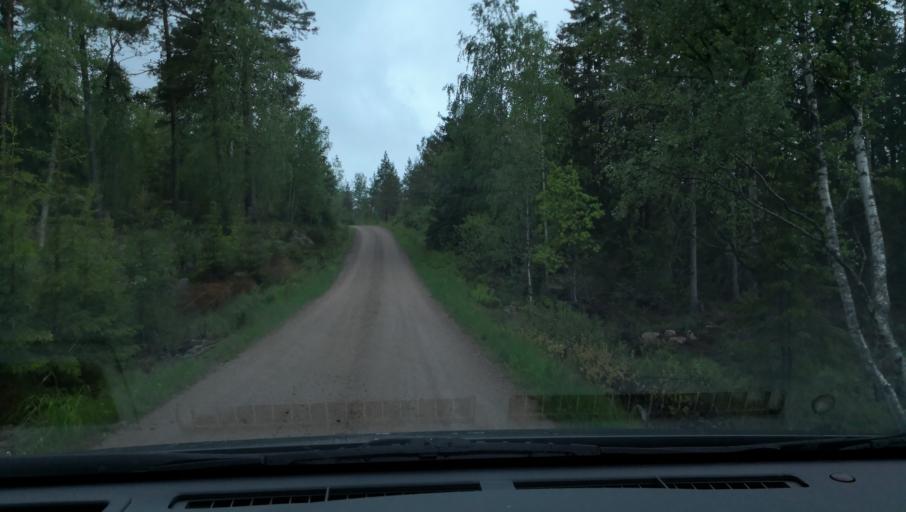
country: SE
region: Uppsala
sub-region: Enkopings Kommun
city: Orsundsbro
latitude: 59.9320
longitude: 17.3282
